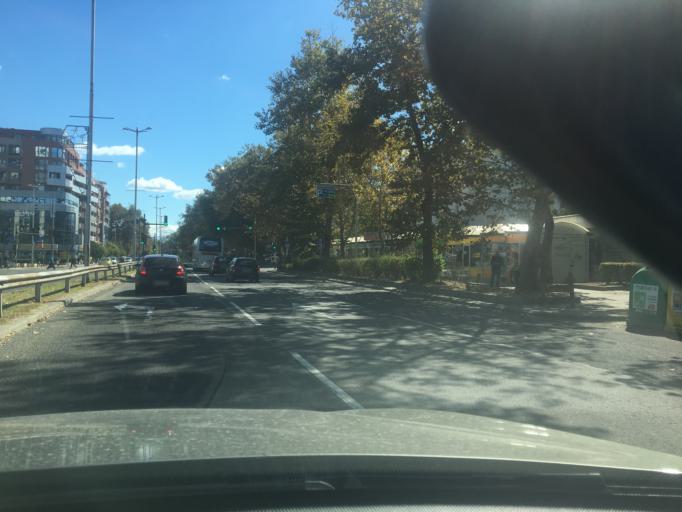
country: BG
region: Burgas
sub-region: Obshtina Burgas
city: Burgas
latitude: 42.5014
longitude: 27.4770
